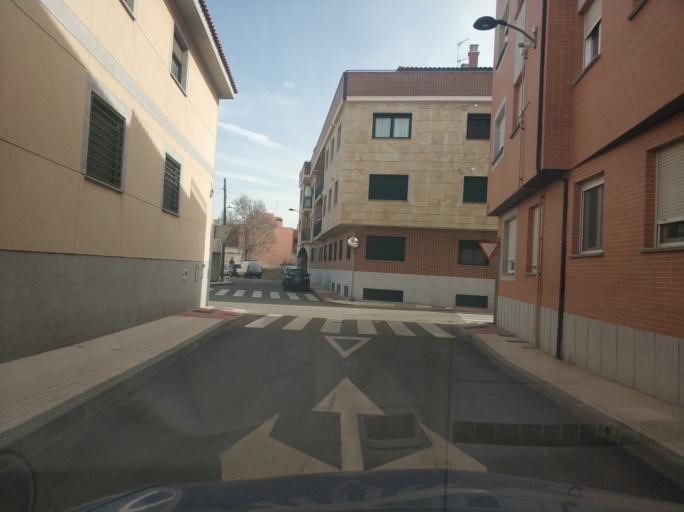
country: ES
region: Castille and Leon
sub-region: Provincia de Salamanca
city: Castellanos de Moriscos
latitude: 41.0176
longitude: -5.5918
